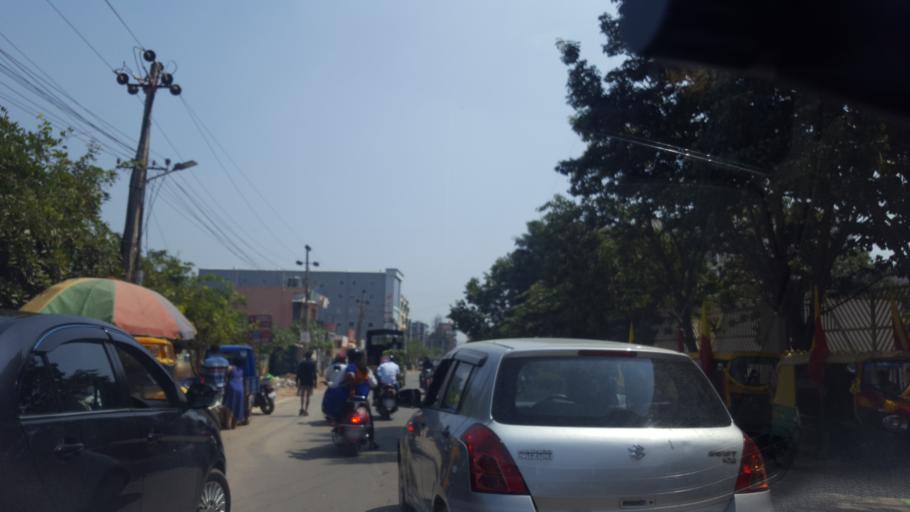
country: IN
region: Karnataka
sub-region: Bangalore Urban
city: Bangalore
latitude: 12.9379
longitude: 77.7003
